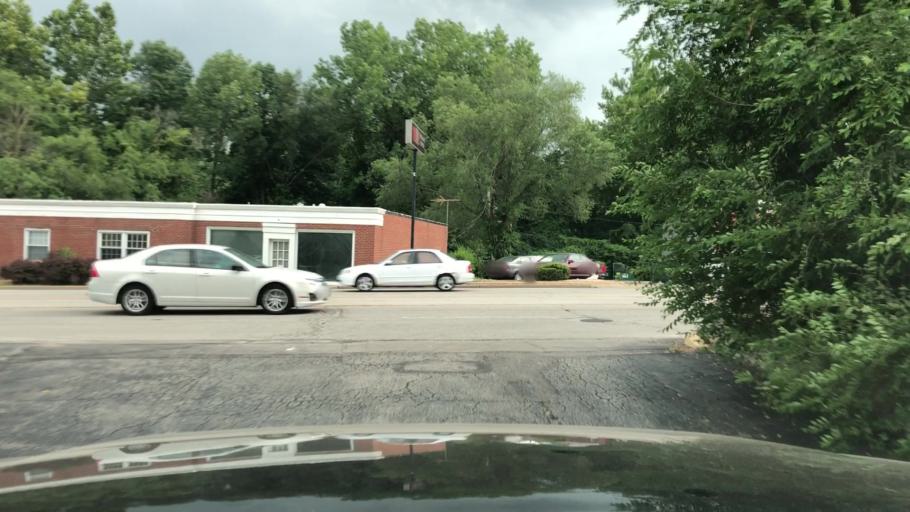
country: US
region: Missouri
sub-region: Saint Charles County
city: Saint Charles
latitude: 38.7843
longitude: -90.5130
